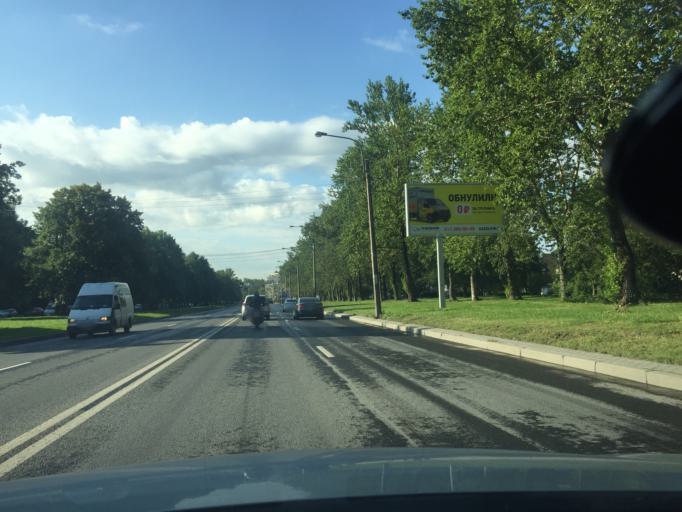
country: RU
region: St.-Petersburg
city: Kupchino
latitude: 59.8432
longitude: 30.3381
